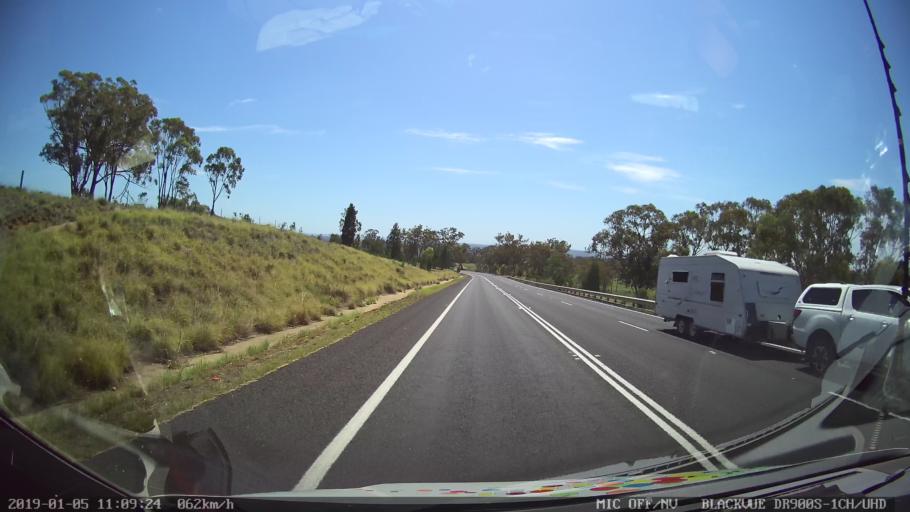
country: AU
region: New South Wales
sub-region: Warrumbungle Shire
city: Coonabarabran
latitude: -31.4135
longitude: 149.2323
